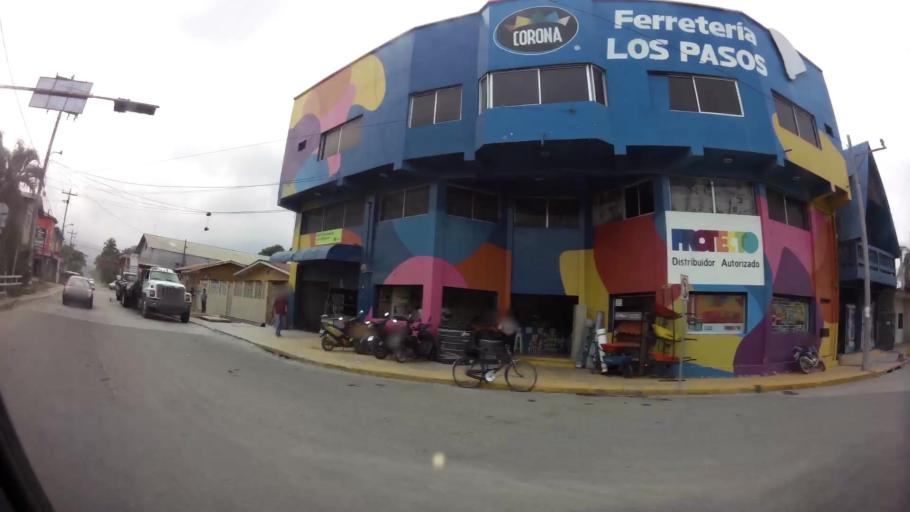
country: HN
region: Yoro
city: El Progreso
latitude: 15.4054
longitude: -87.8062
